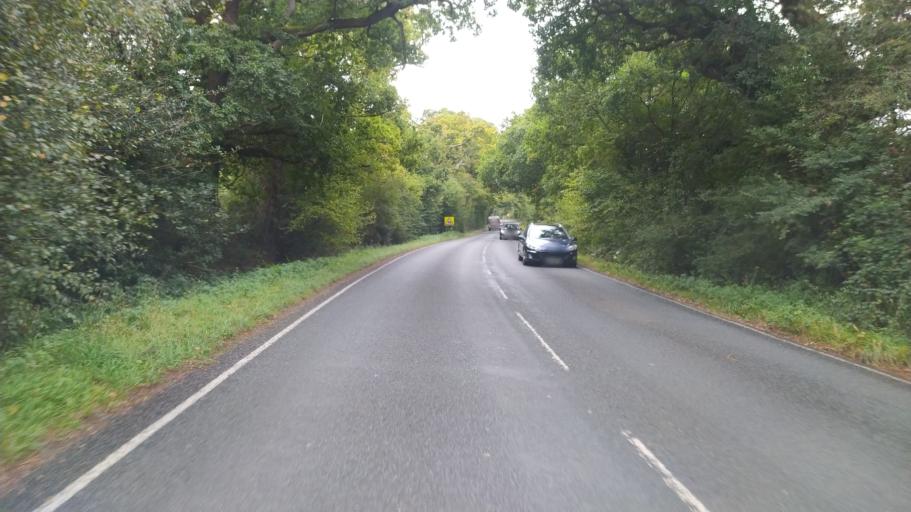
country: GB
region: England
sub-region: Hampshire
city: Brockenhurst
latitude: 50.8153
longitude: -1.5718
